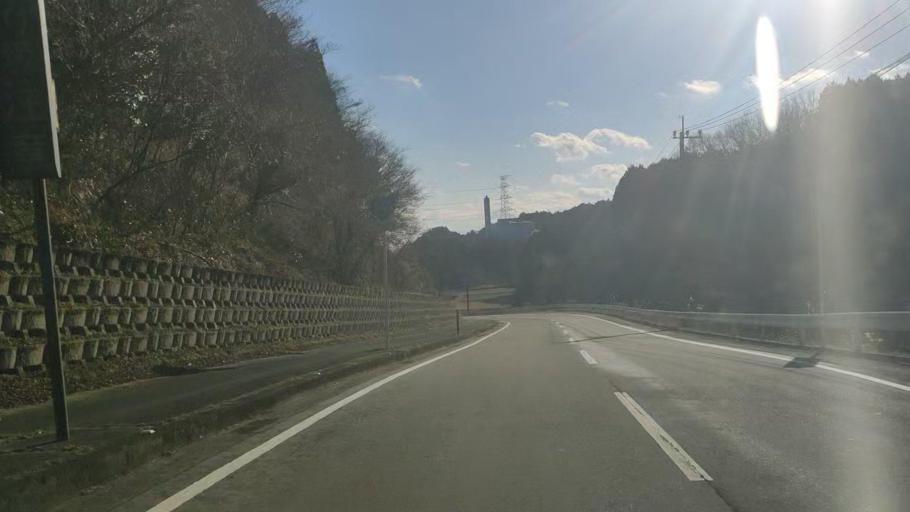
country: JP
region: Saga Prefecture
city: Kanzakimachi-kanzaki
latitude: 33.4036
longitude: 130.2728
